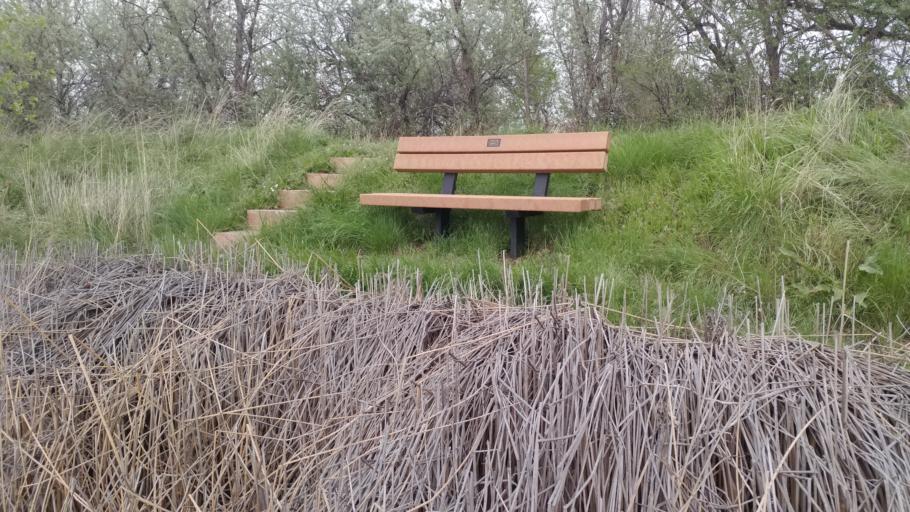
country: US
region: Colorado
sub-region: Boulder County
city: Gunbarrel
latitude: 40.0469
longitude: -105.1804
